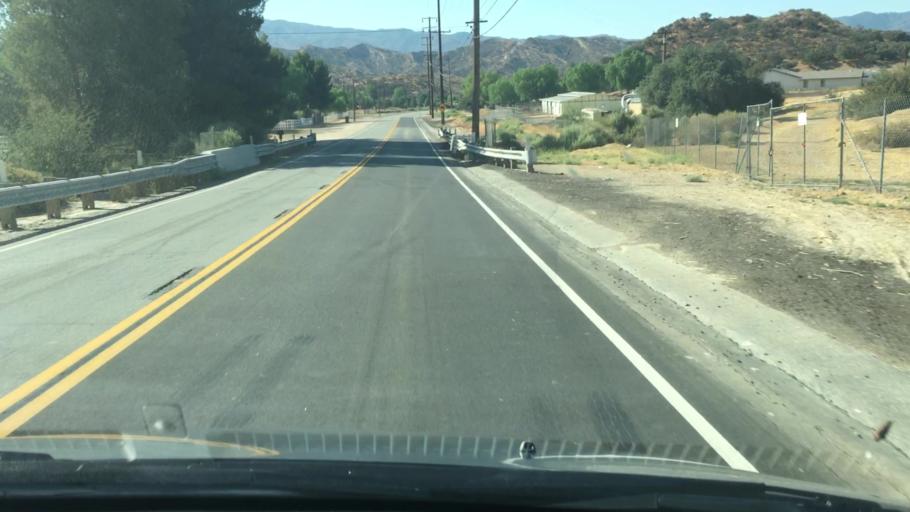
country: US
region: California
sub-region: Los Angeles County
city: Agua Dulce
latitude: 34.4659
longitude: -118.4238
